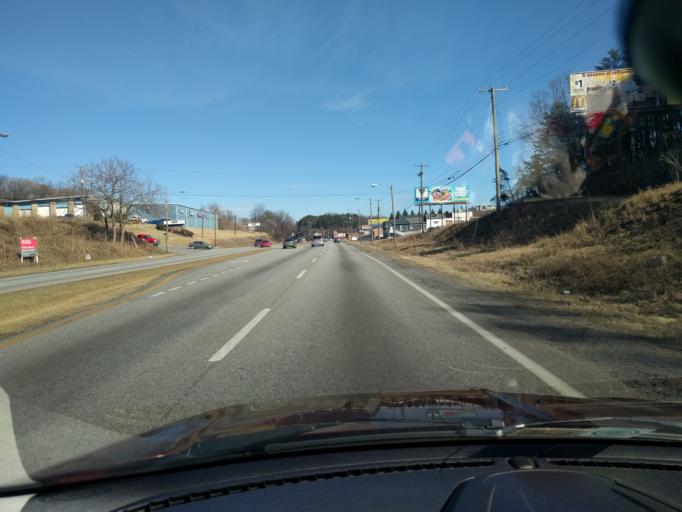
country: US
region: Virginia
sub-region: Roanoke County
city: Vinton
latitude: 37.2981
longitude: -79.8970
